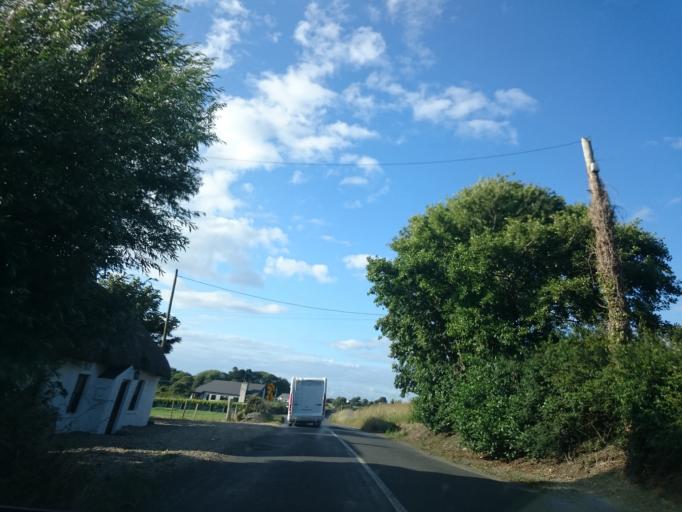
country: IE
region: Leinster
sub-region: Loch Garman
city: Loch Garman
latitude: 52.1932
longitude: -6.5594
